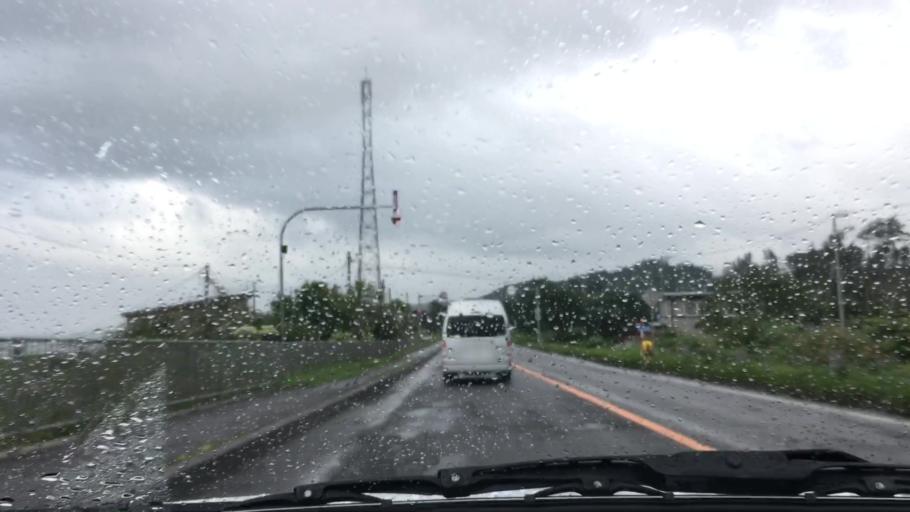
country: JP
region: Hokkaido
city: Nanae
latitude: 42.2339
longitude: 140.3221
